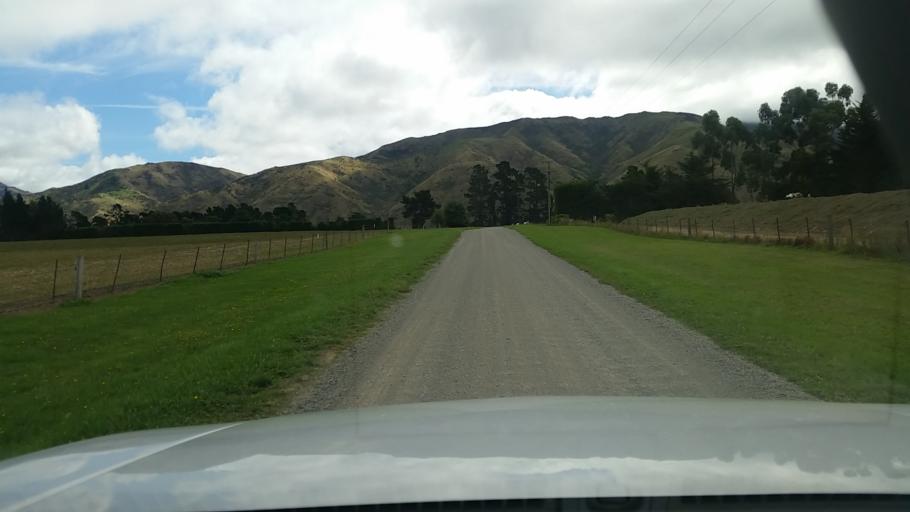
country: NZ
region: Marlborough
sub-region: Marlborough District
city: Blenheim
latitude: -41.6976
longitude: 173.9512
